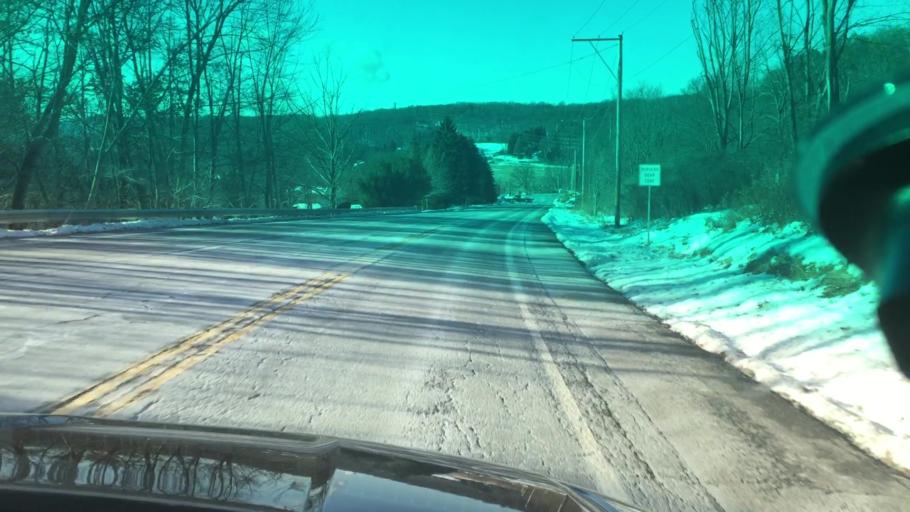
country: US
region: Pennsylvania
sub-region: Luzerne County
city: Harleigh
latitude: 41.0192
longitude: -75.9587
